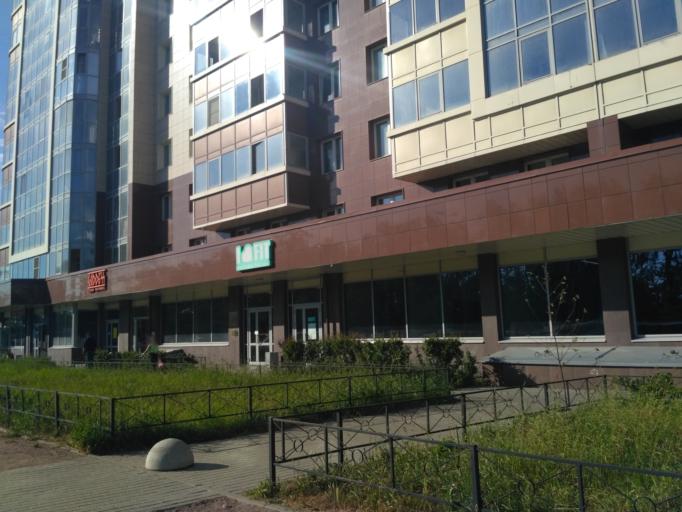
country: RU
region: St.-Petersburg
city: Kushelevka
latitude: 59.9837
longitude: 30.3705
